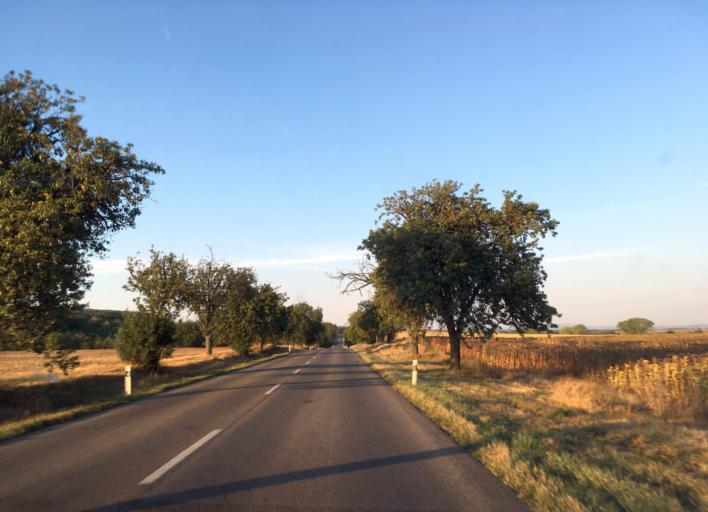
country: HU
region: Komarom-Esztergom
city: Neszmely
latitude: 47.8082
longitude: 18.3348
